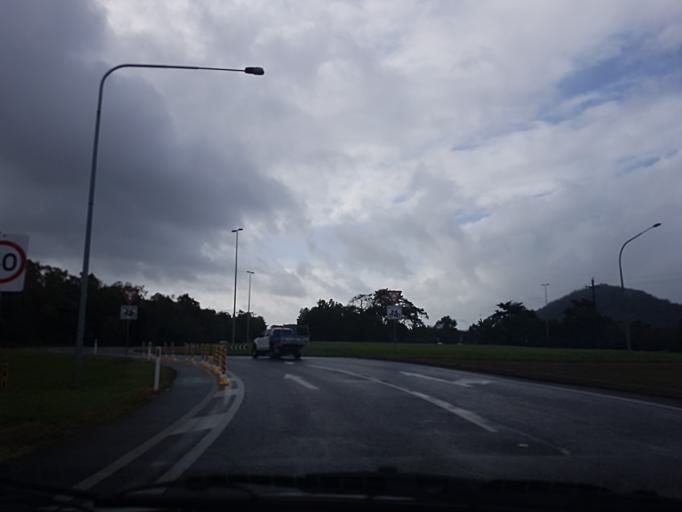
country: AU
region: Queensland
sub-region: Cairns
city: Trinity Beach
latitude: -16.8121
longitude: 145.6929
